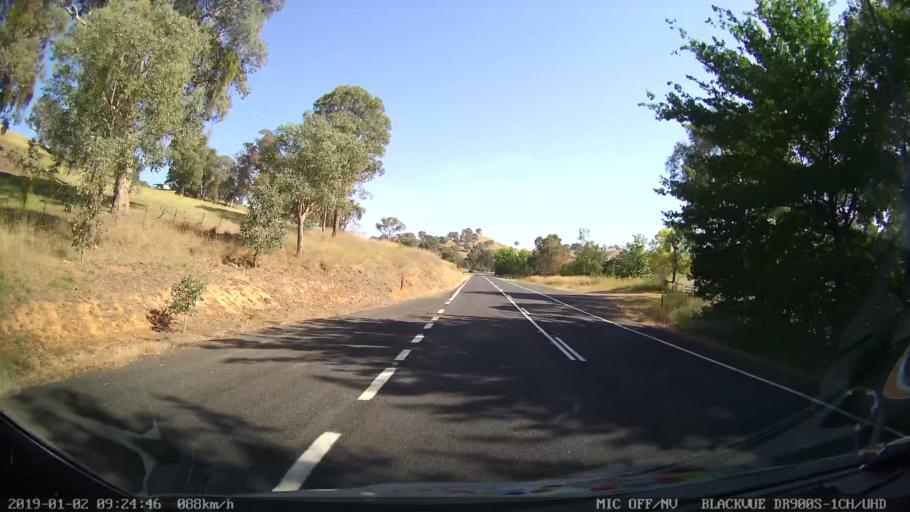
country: AU
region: New South Wales
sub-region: Tumut Shire
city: Tumut
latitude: -35.3727
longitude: 148.2918
